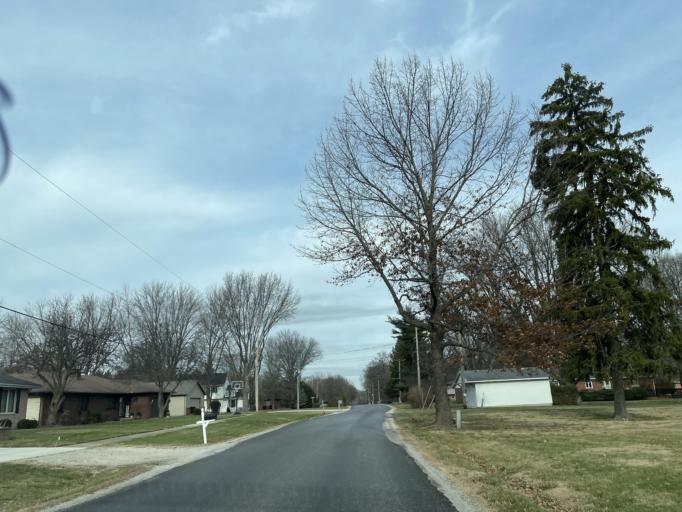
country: US
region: Illinois
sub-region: Sangamon County
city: Leland Grove
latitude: 39.8043
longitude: -89.7298
